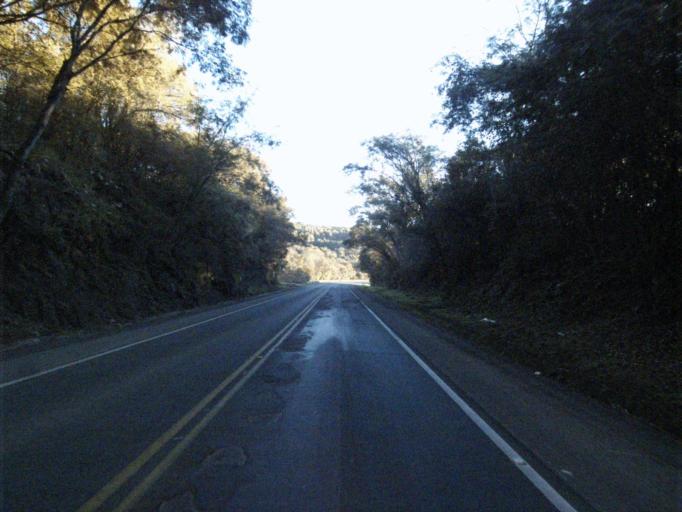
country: BR
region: Santa Catarina
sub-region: Chapeco
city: Chapeco
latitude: -26.8322
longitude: -53.0292
